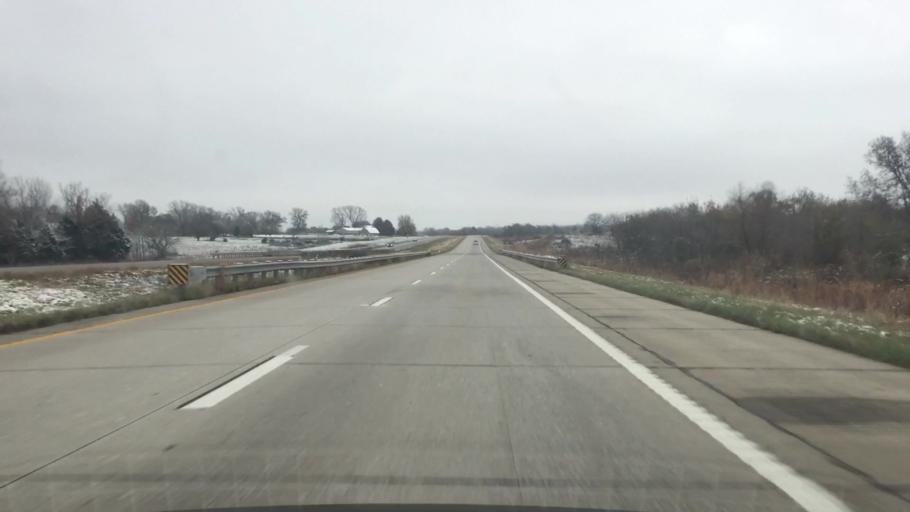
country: US
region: Missouri
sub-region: Saint Clair County
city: Osceola
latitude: 38.1961
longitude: -93.7450
